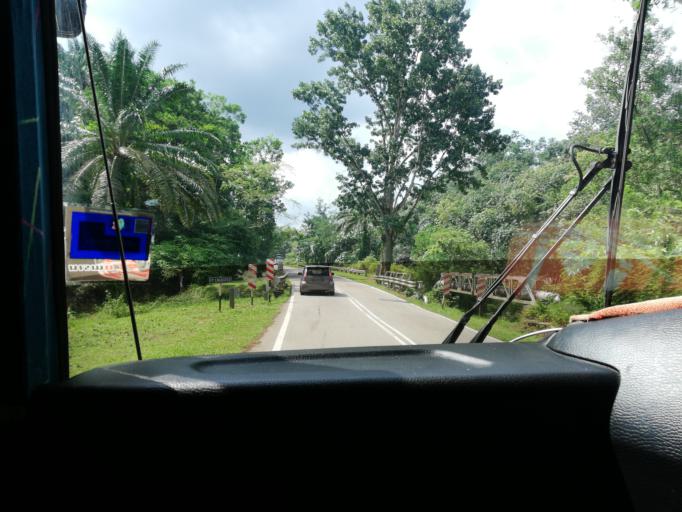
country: MY
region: Kedah
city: Kulim
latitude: 5.3150
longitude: 100.6030
